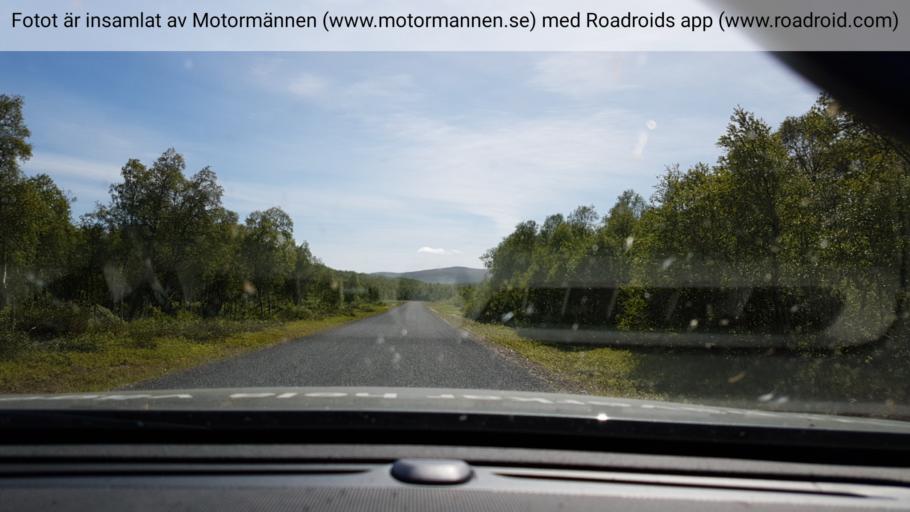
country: NO
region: Nordland
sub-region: Hattfjelldal
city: Hattfjelldal
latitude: 65.4246
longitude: 14.6558
